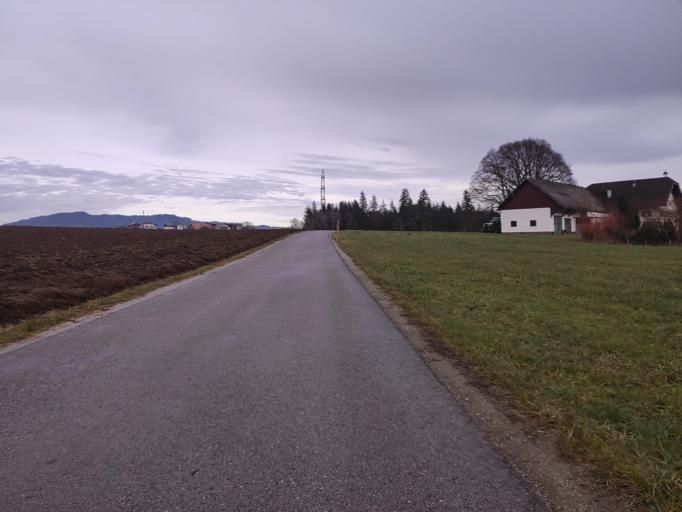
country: AT
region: Salzburg
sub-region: Politischer Bezirk Salzburg-Umgebung
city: Elixhausen
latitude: 47.8872
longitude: 13.0547
